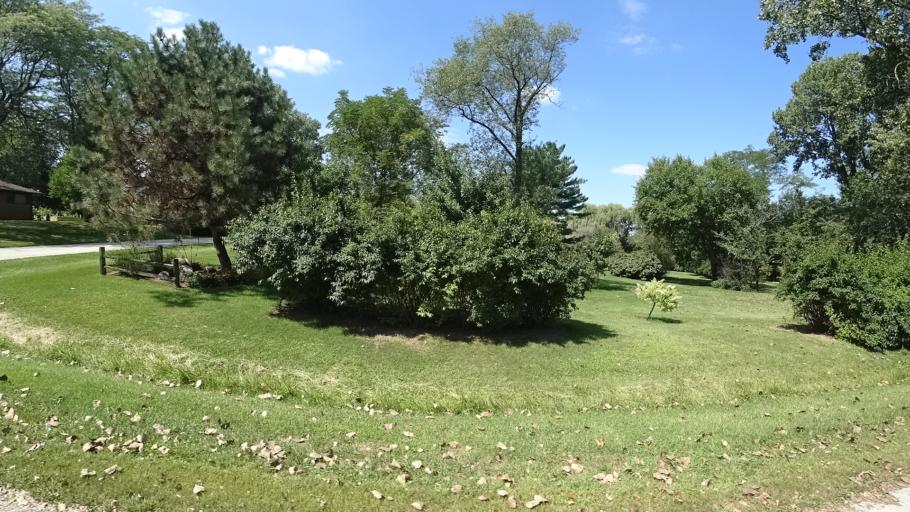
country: US
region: Illinois
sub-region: Cook County
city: Orland Park
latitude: 41.6285
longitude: -87.8456
